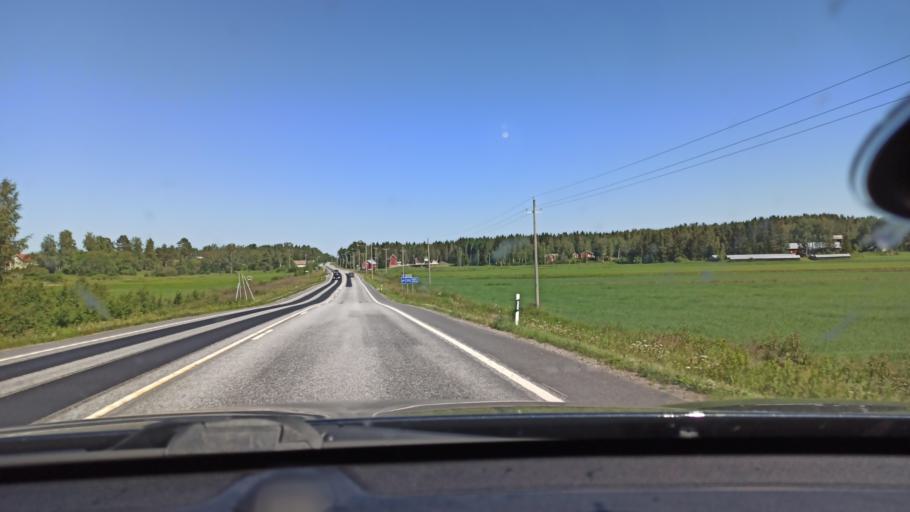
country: FI
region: Ostrobothnia
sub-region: Vaasa
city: Voera
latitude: 63.2089
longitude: 22.1652
